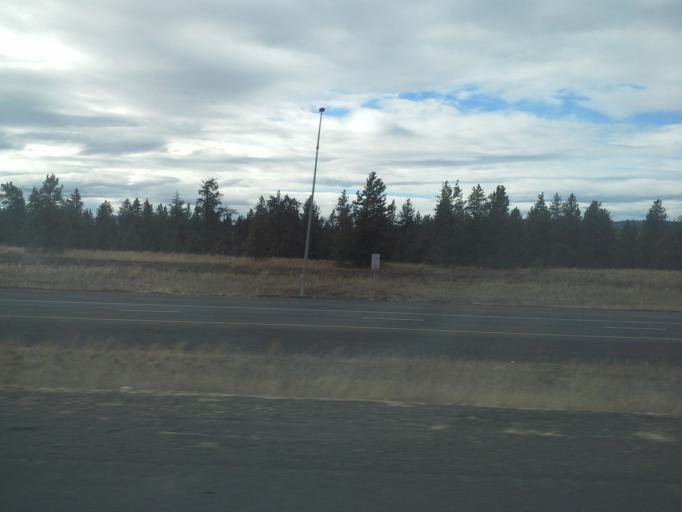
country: US
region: Oregon
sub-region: Union County
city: La Grande
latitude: 45.3674
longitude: -118.2863
